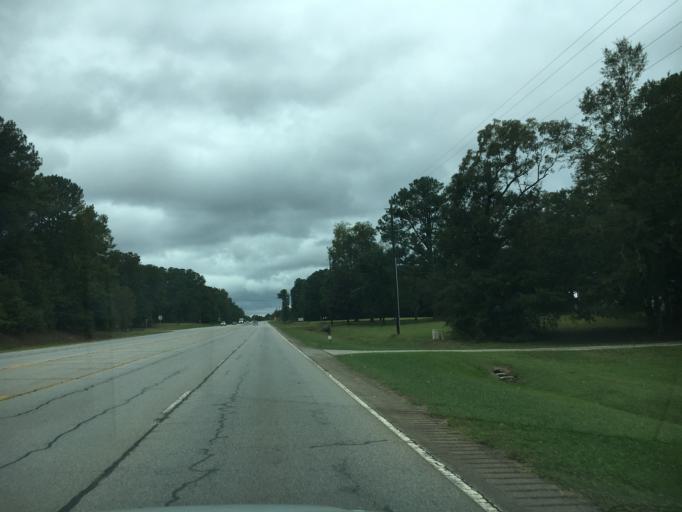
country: US
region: Georgia
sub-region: Wilkes County
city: Washington
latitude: 33.7172
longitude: -82.7052
